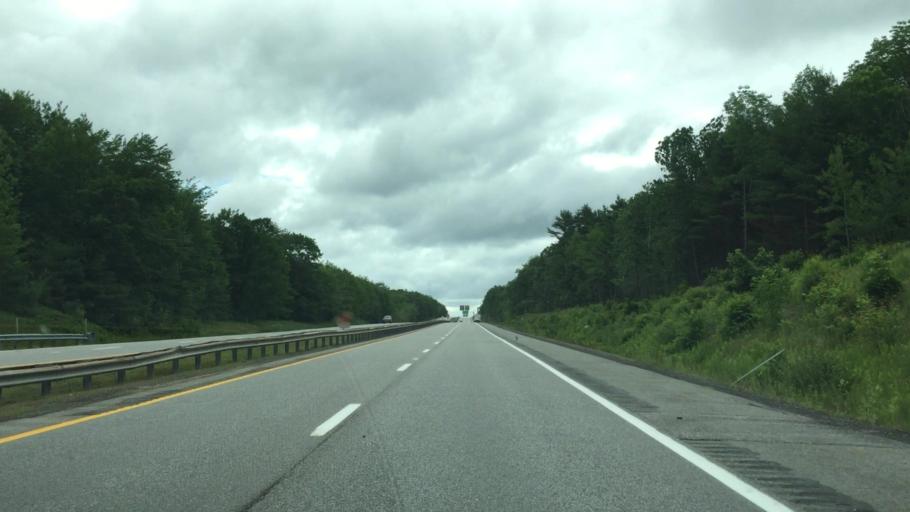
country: US
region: Maine
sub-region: Cumberland County
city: Falmouth
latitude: 43.7301
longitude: -70.2762
